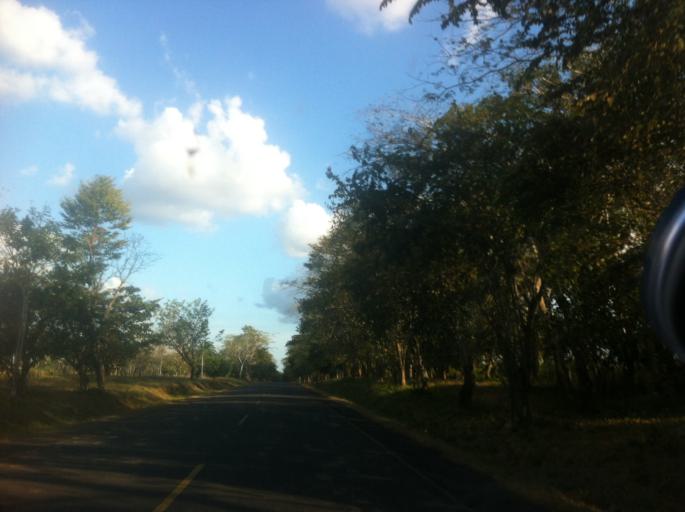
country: NI
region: Rio San Juan
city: El Almendro
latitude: 11.6011
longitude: -84.8594
